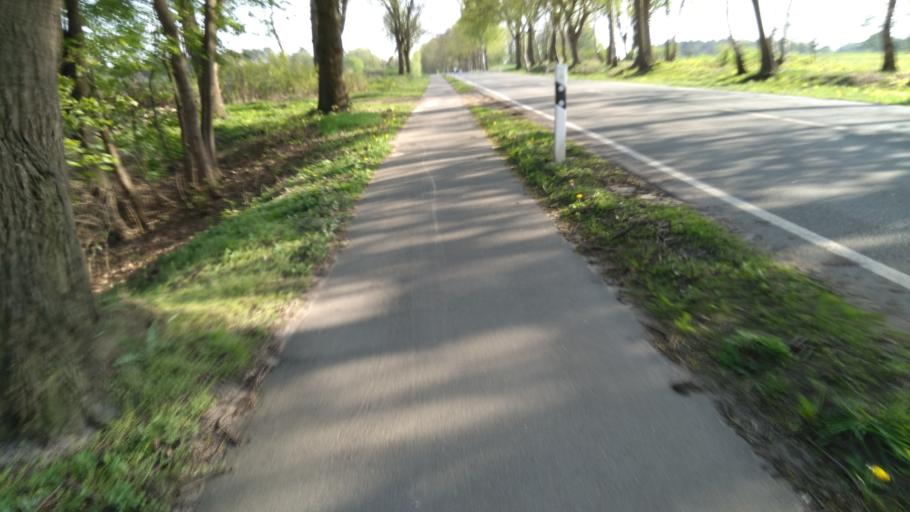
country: DE
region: Lower Saxony
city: Buxtehude
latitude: 53.4582
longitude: 9.6967
